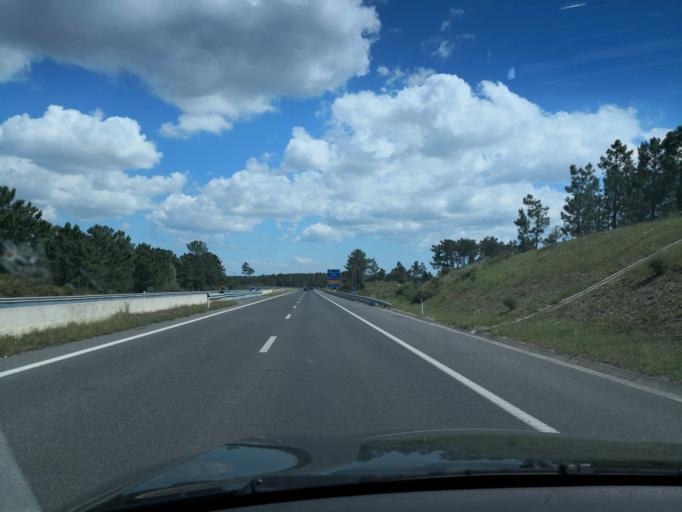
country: PT
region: Setubal
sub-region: Seixal
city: Corroios
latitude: 38.6098
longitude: -9.1521
